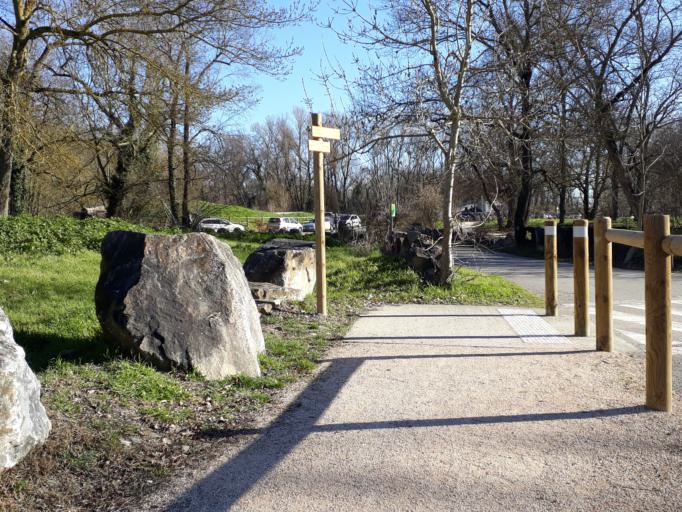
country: FR
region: Midi-Pyrenees
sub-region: Departement de la Haute-Garonne
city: Fenouillet
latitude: 43.6654
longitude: 1.3927
